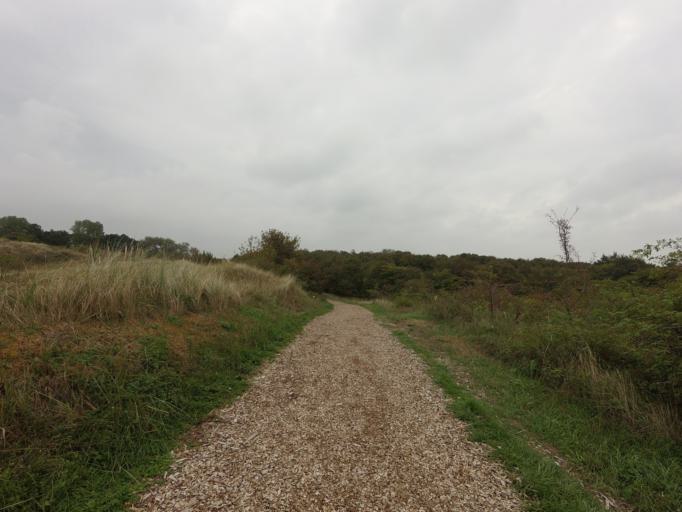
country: NL
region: Friesland
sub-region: Gemeente Schiermonnikoog
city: Schiermonnikoog
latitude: 53.4862
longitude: 6.1831
